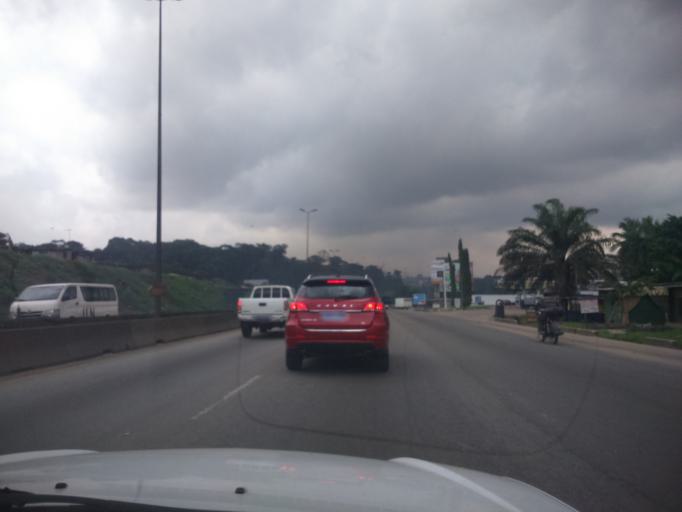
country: CI
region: Lagunes
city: Abidjan
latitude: 5.3592
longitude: -4.0611
